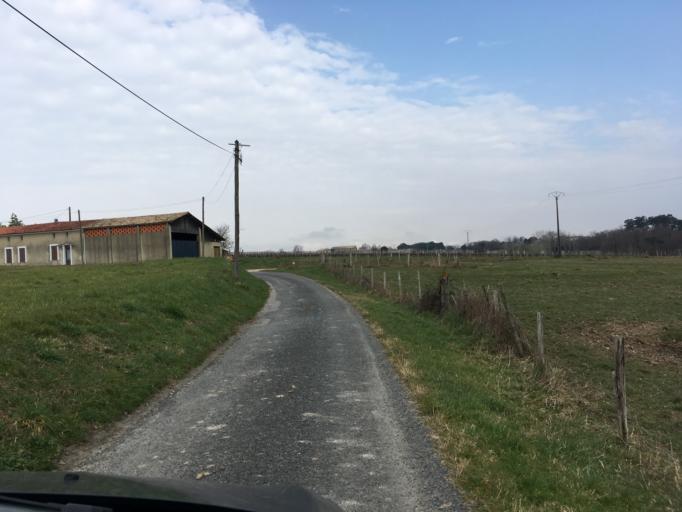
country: FR
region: Poitou-Charentes
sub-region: Departement de la Charente-Maritime
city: Mirambeau
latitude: 45.3334
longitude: -0.5867
